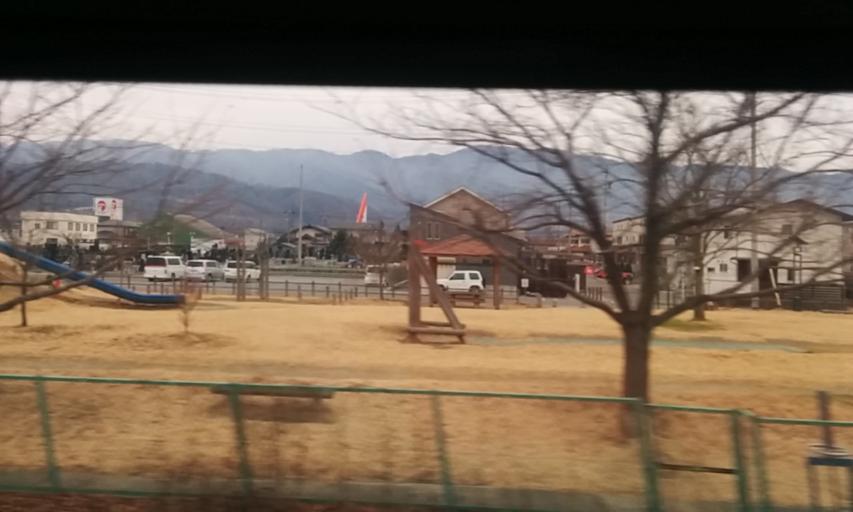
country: JP
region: Nagano
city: Matsumoto
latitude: 36.1945
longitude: 137.9636
